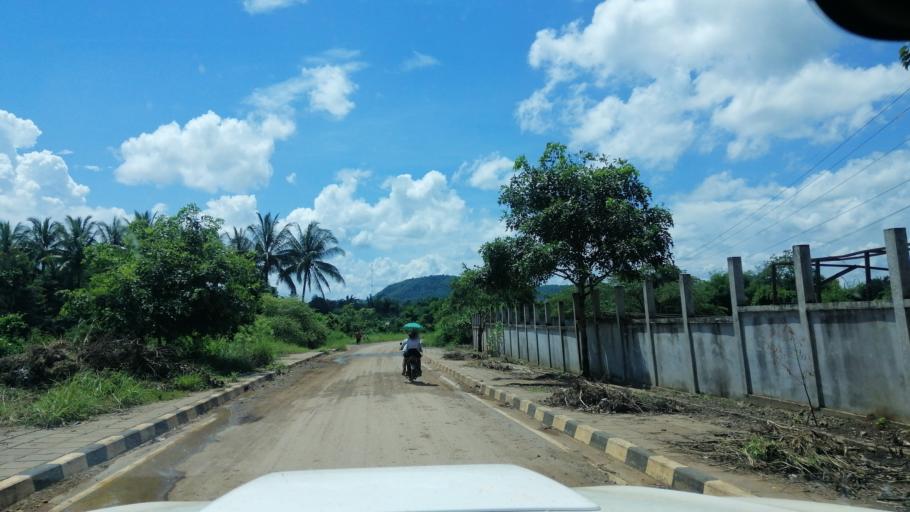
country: TH
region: Uttaradit
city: Ban Khok
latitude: 18.1351
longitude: 101.2770
